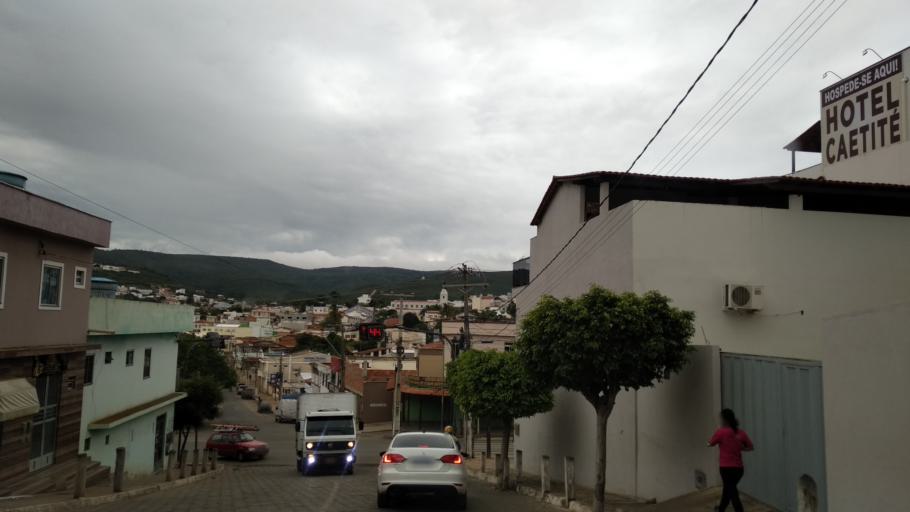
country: BR
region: Bahia
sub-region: Caetite
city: Caetite
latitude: -14.0637
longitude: -42.4847
